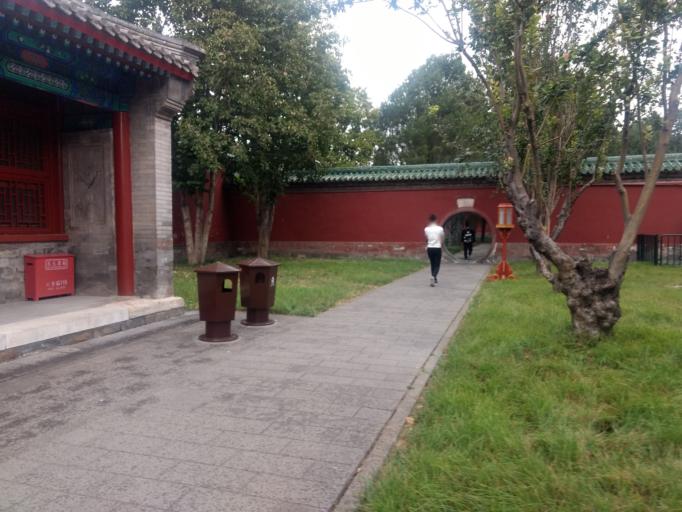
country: CN
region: Beijing
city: Longtan
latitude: 39.8786
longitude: 116.4003
